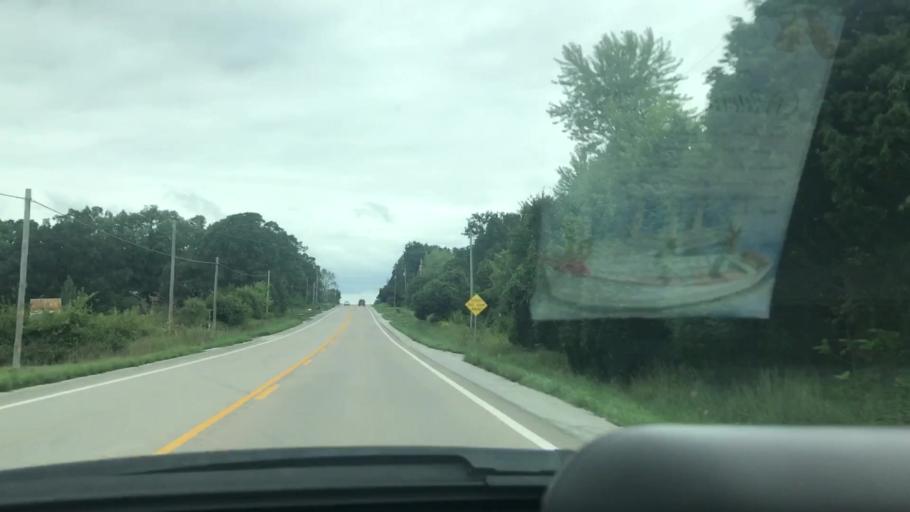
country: US
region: Missouri
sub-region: Dallas County
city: Buffalo
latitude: 37.7001
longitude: -93.1066
